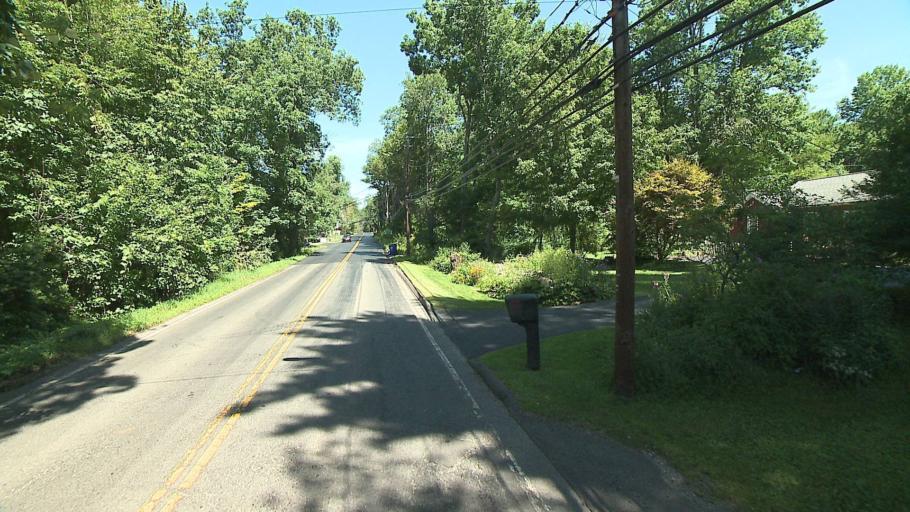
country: US
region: Connecticut
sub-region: Hartford County
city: West Simsbury
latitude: 41.8934
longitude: -72.8927
